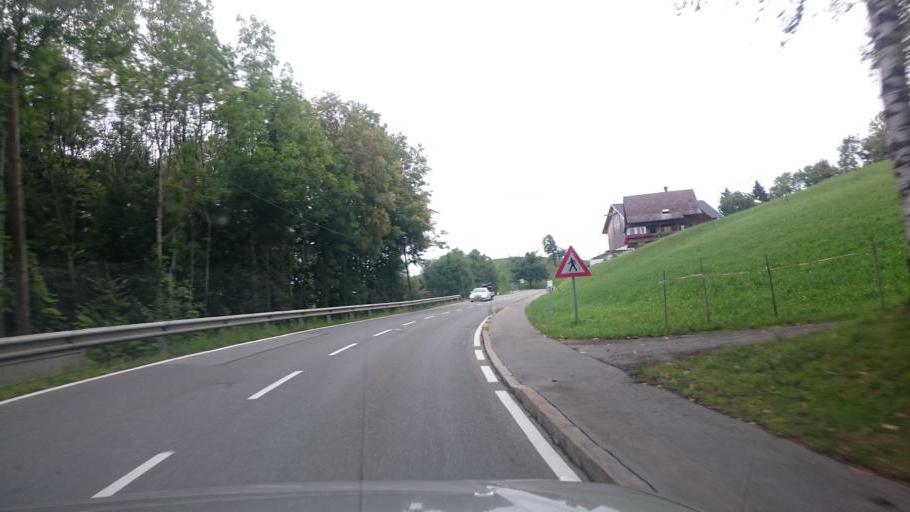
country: AT
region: Vorarlberg
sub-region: Politischer Bezirk Dornbirn
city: Dornbirn
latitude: 47.4208
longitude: 9.7694
